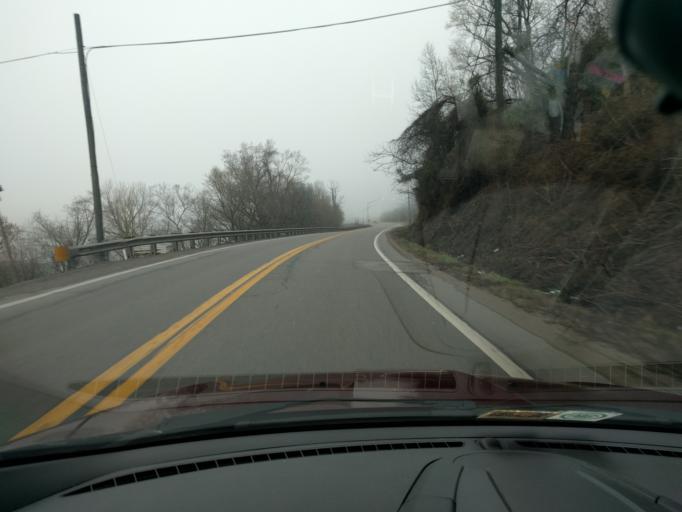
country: US
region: West Virginia
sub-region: Kanawha County
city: Chesapeake
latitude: 38.2031
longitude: -81.4807
